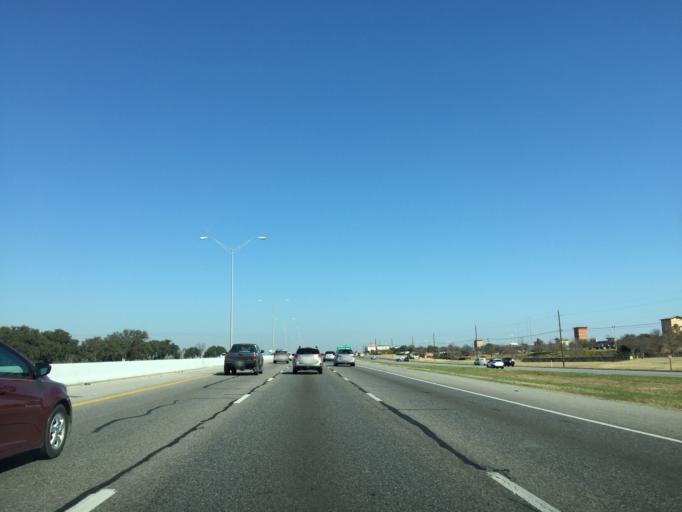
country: US
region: Texas
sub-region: Williamson County
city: Round Rock
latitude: 30.5622
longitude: -97.6925
